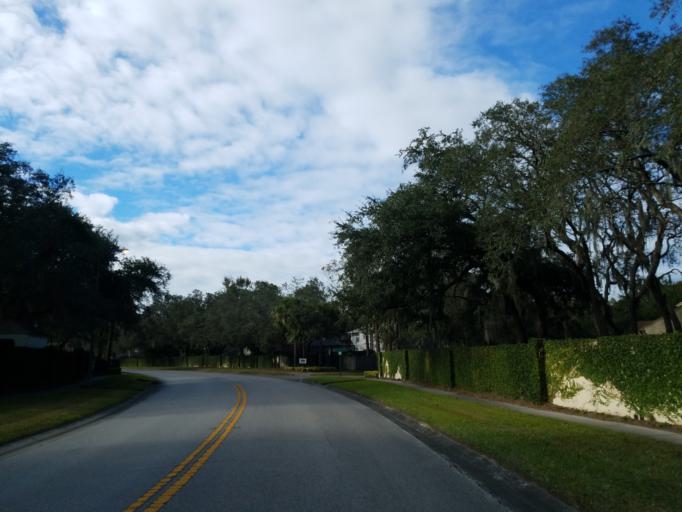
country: US
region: Florida
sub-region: Hillsborough County
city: Bloomingdale
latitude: 27.8856
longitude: -82.2562
